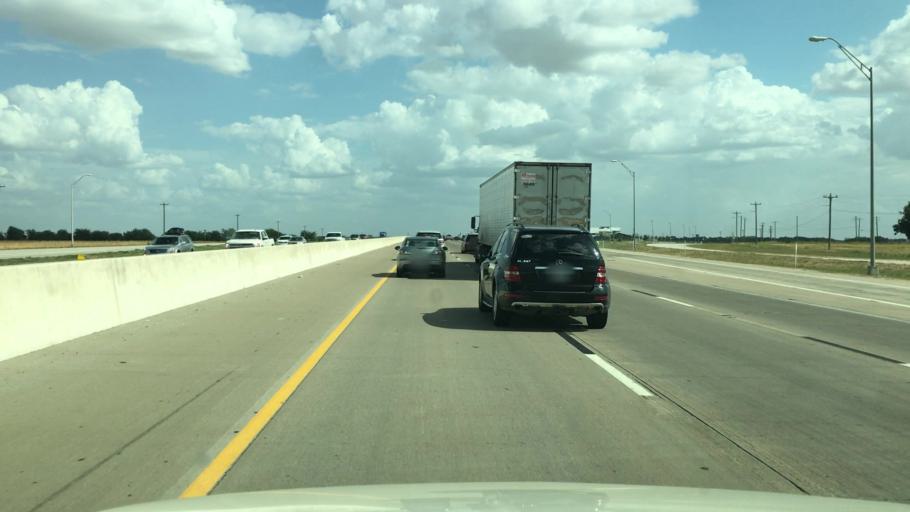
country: US
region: Texas
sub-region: Hill County
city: Hillsboro
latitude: 31.9317
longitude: -97.1044
